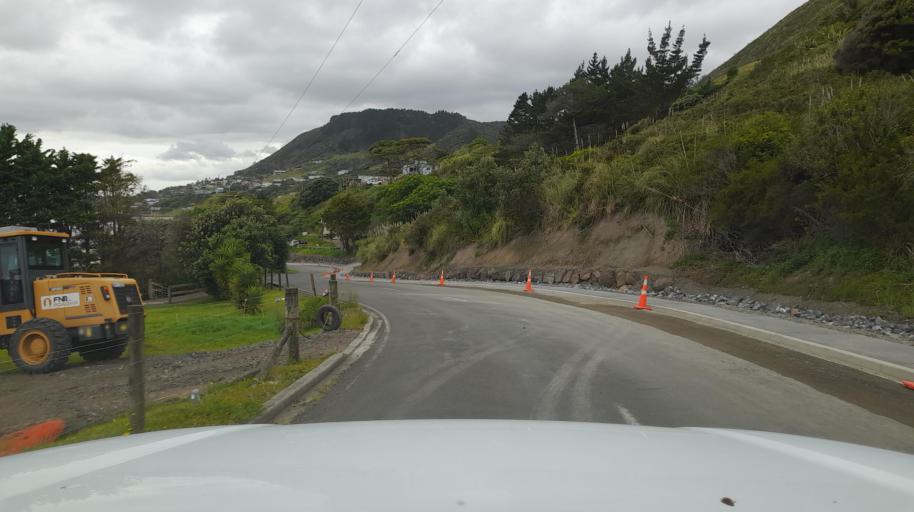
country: NZ
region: Northland
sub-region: Far North District
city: Ahipara
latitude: -35.1798
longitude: 173.1287
